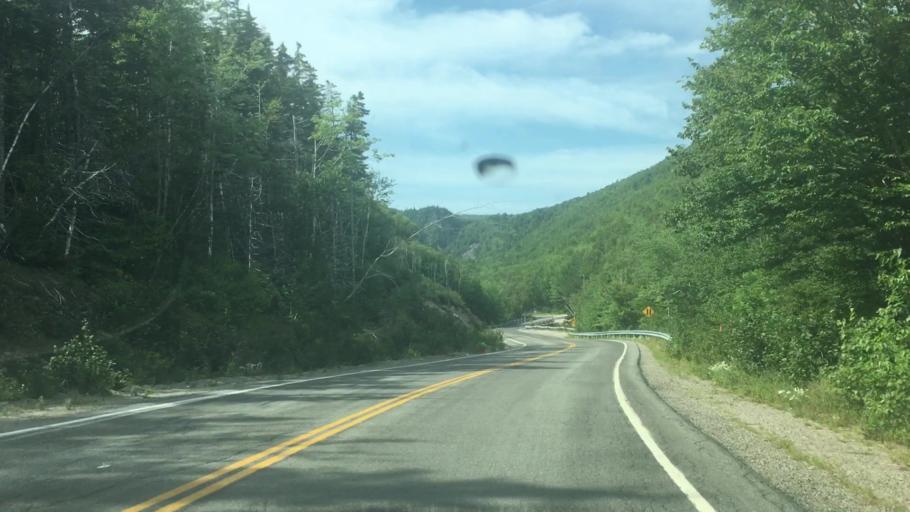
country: CA
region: Nova Scotia
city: Sydney Mines
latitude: 46.5823
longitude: -60.3939
